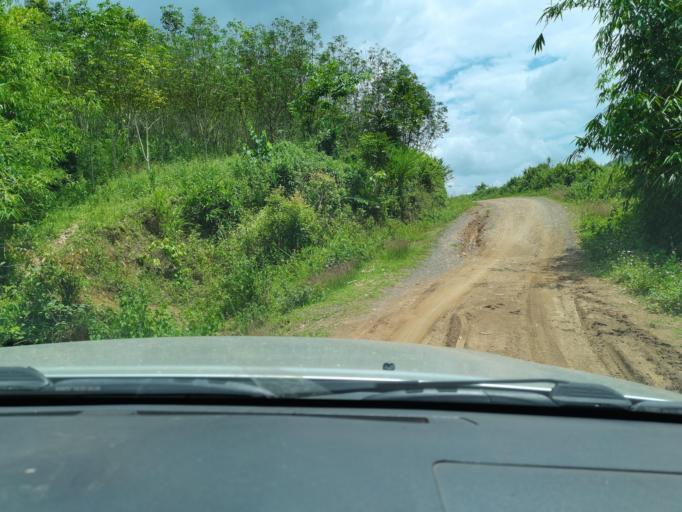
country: LA
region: Loungnamtha
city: Muang Long
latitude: 20.7209
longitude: 101.0142
